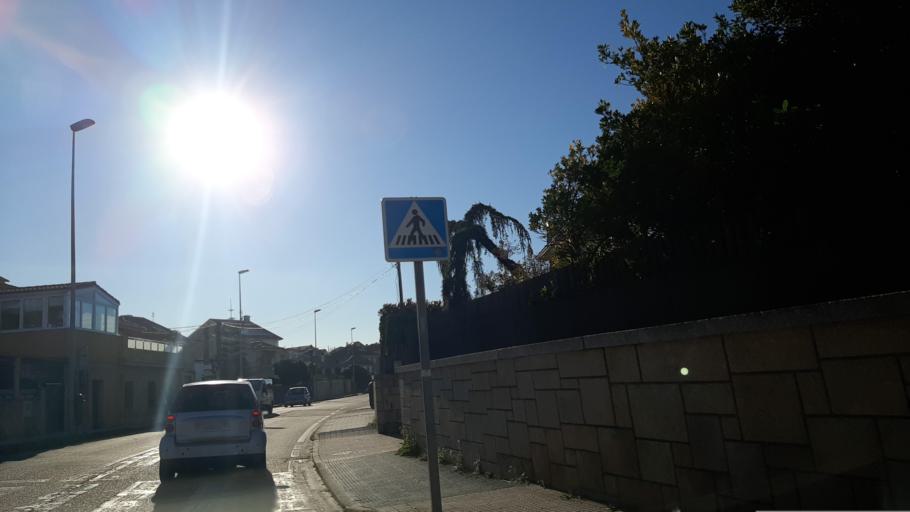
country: ES
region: Galicia
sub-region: Provincia de Pontevedra
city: Nigran
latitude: 42.2002
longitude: -8.7852
